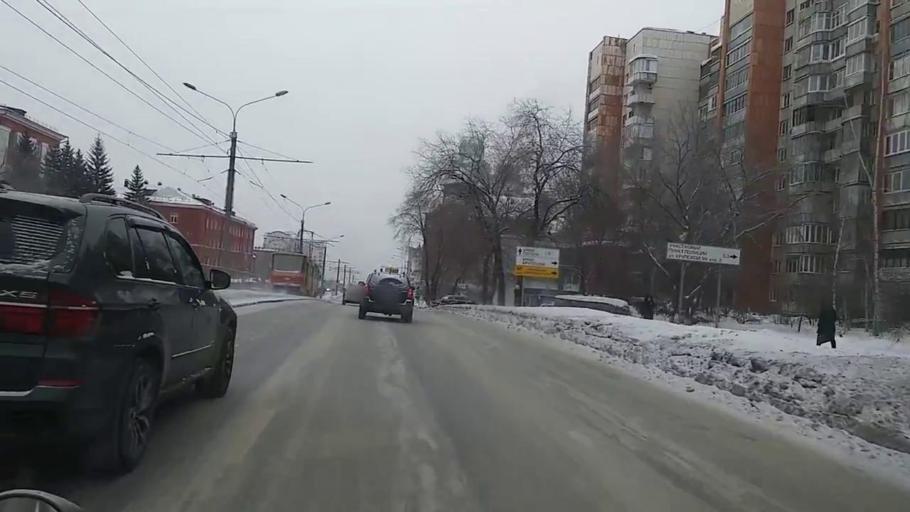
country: RU
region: Altai Krai
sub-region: Gorod Barnaulskiy
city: Barnaul
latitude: 53.3439
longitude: 83.7674
